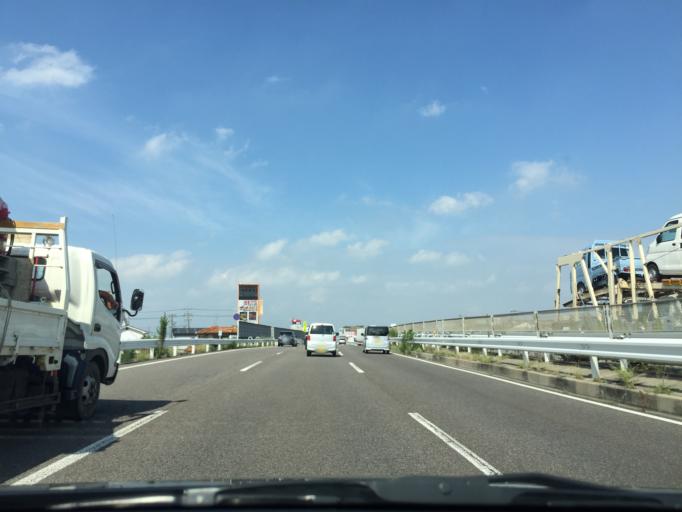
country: JP
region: Gifu
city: Kasamatsucho
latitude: 35.3890
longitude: 136.7429
